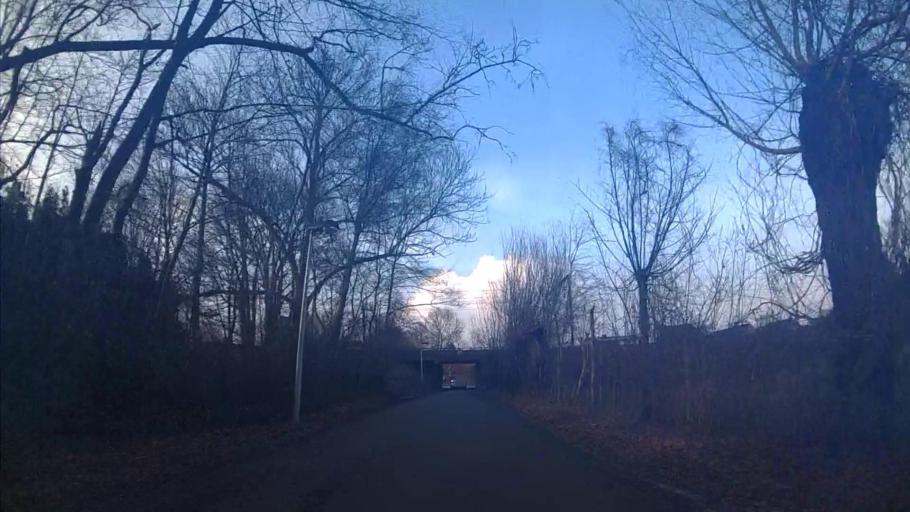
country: BE
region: Flanders
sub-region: Provincie Oost-Vlaanderen
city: Destelbergen
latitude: 51.0679
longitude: 3.7856
